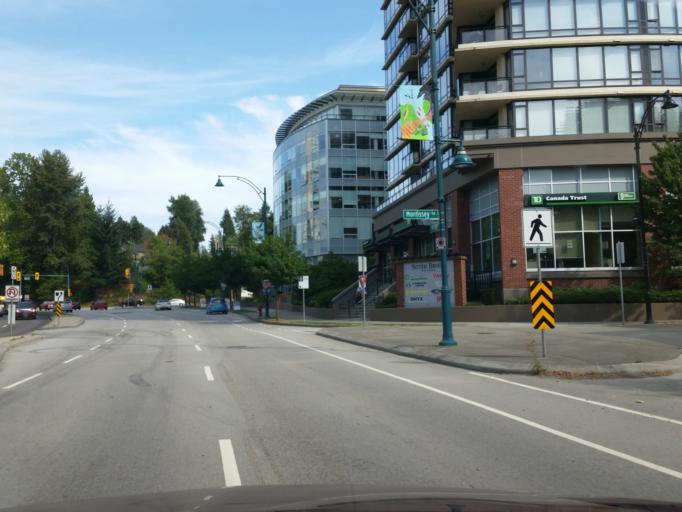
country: CA
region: British Columbia
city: Port Moody
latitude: 49.2805
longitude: -122.8293
